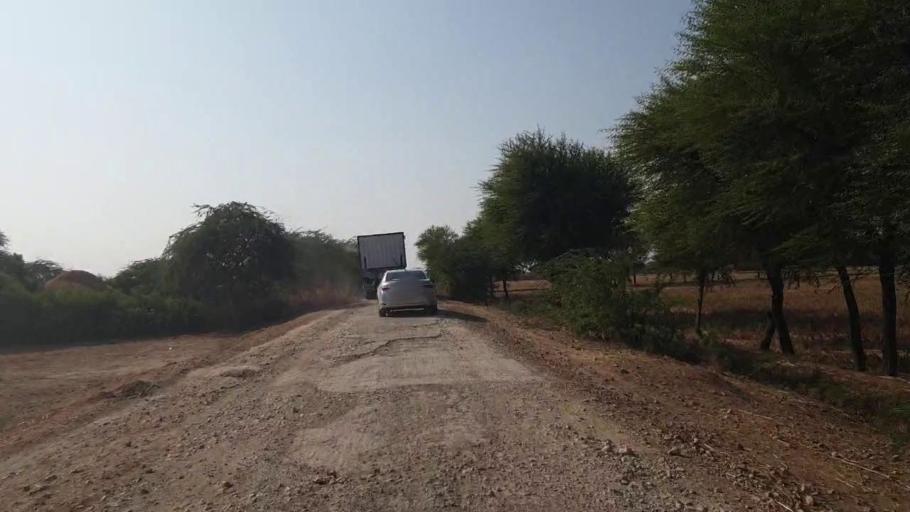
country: PK
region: Sindh
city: Matli
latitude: 24.9512
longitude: 68.6870
